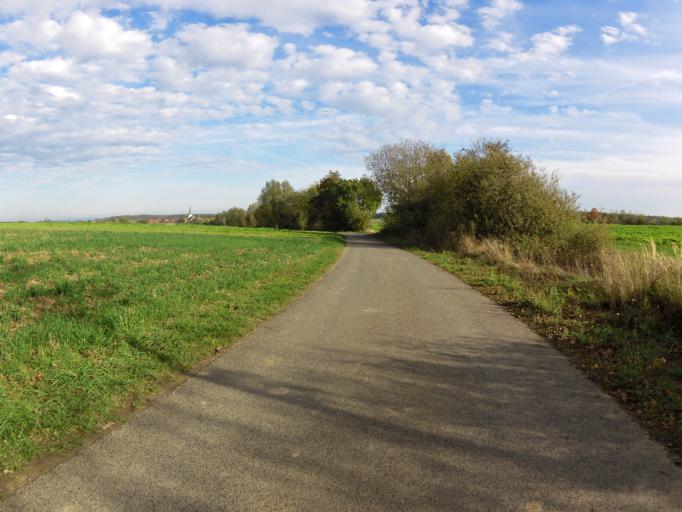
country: DE
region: Bavaria
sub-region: Regierungsbezirk Unterfranken
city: Biebelried
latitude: 49.7276
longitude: 10.0753
